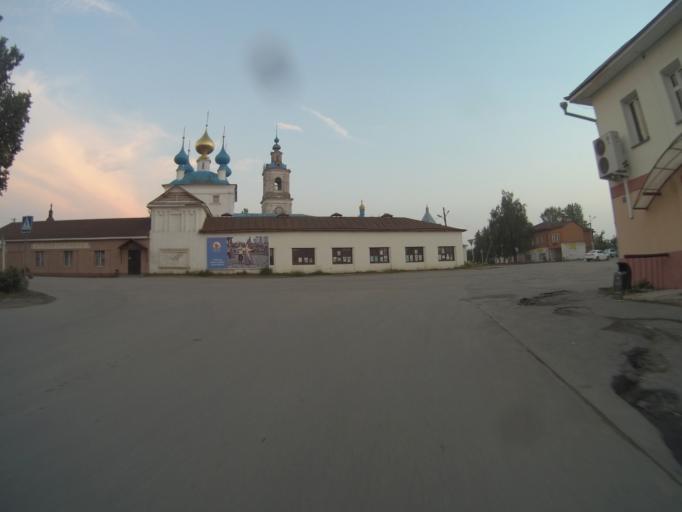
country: RU
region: Vladimir
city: Stavrovo
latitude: 56.1338
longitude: 40.0154
